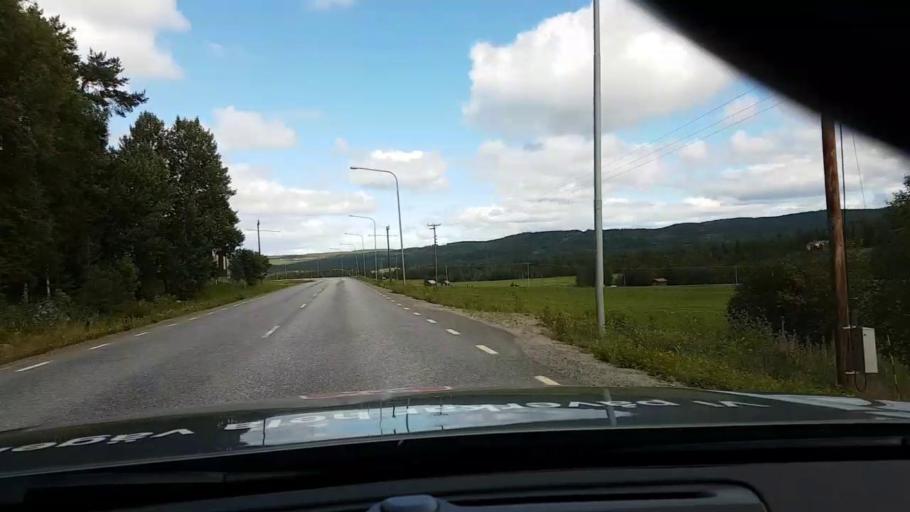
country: SE
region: Vaesternorrland
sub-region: OErnskoeldsviks Kommun
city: Bredbyn
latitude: 63.4951
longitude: 18.0816
